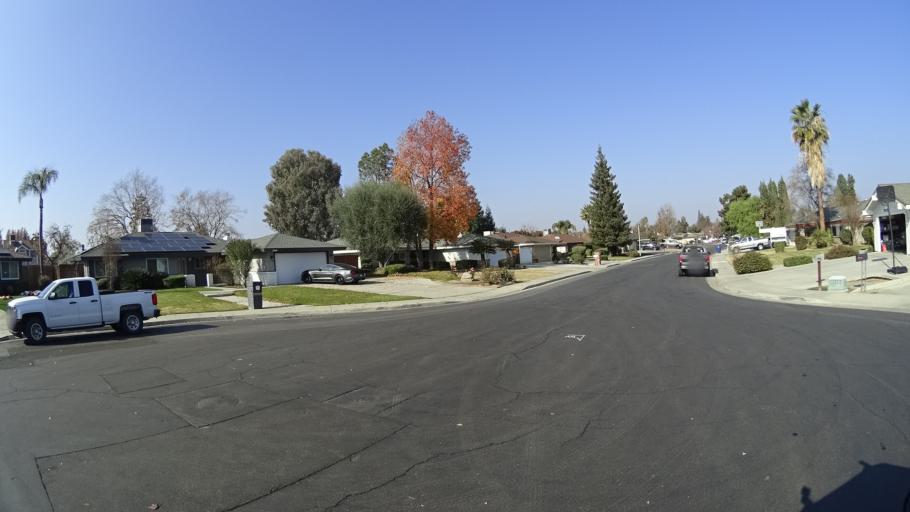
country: US
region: California
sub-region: Kern County
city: Greenacres
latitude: 35.3246
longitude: -119.0806
